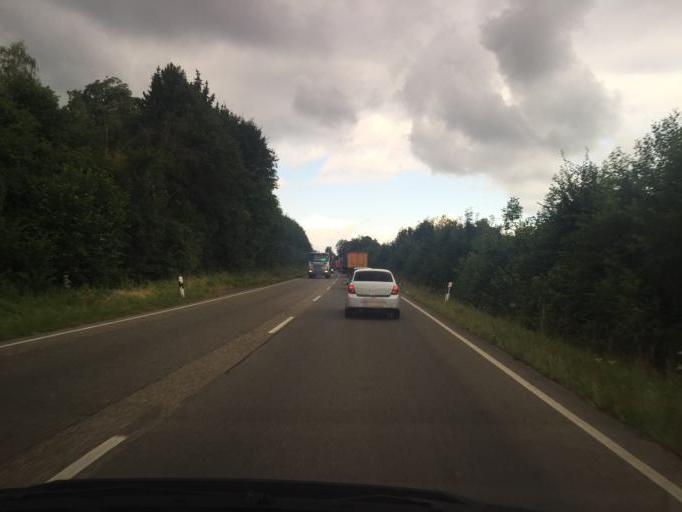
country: DE
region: Baden-Wuerttemberg
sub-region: Karlsruhe Region
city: Bruchsal
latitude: 49.1150
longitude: 8.6167
